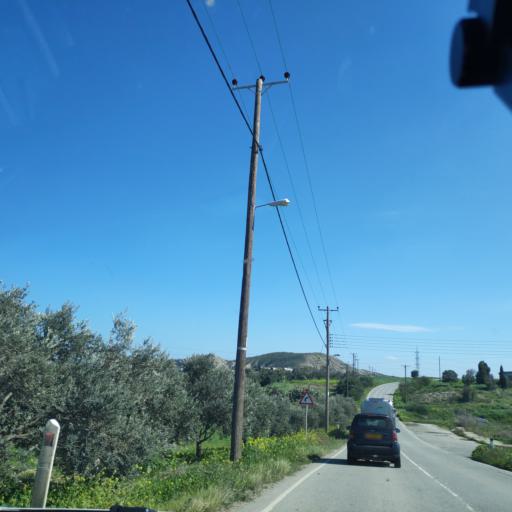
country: CY
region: Lefkosia
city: Tseri
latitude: 35.0230
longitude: 33.3282
